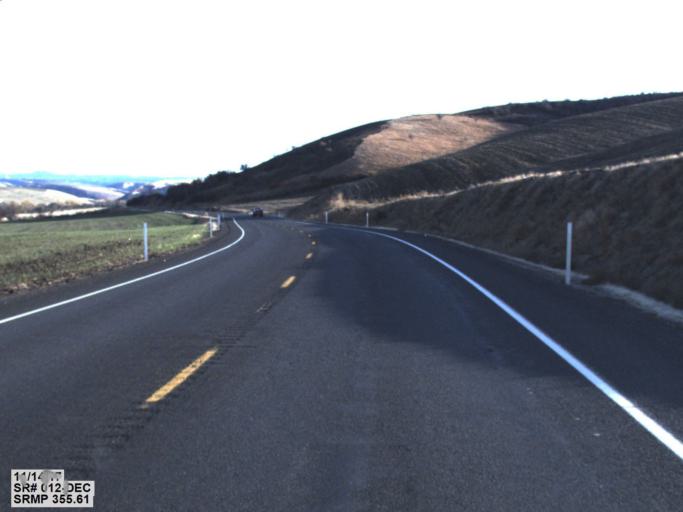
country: US
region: Washington
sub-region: Walla Walla County
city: Waitsburg
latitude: 46.2427
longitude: -118.1447
